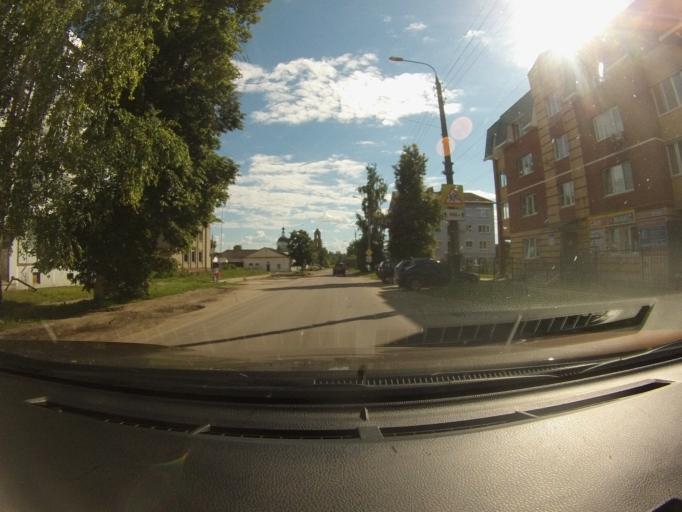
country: RU
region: Orjol
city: Mtsensk
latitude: 53.2781
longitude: 36.5704
